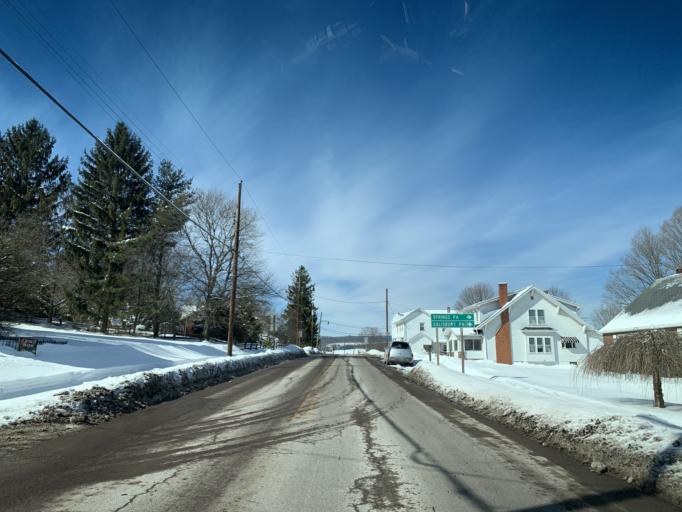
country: US
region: Pennsylvania
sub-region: Somerset County
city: Meyersdale
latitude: 39.6977
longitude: -79.1607
